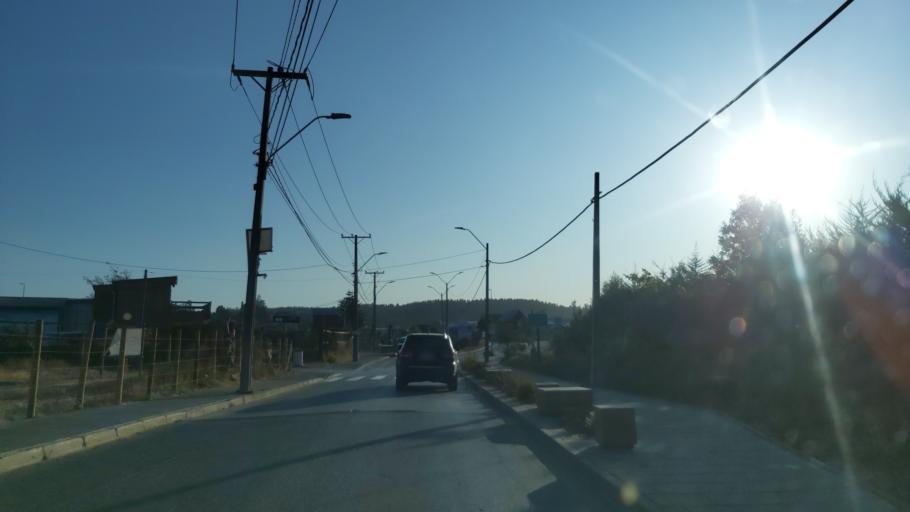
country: CL
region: Biobio
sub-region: Provincia de Concepcion
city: Tome
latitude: -36.5444
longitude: -72.9315
